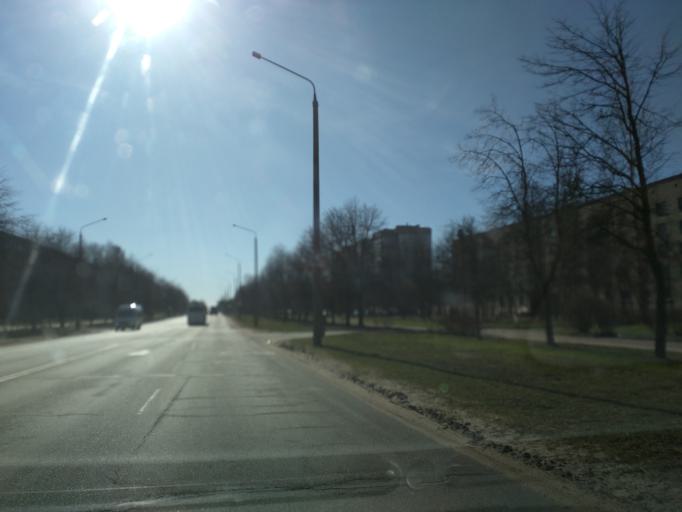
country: BY
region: Mogilev
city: Babruysk
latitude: 53.1763
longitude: 29.1922
